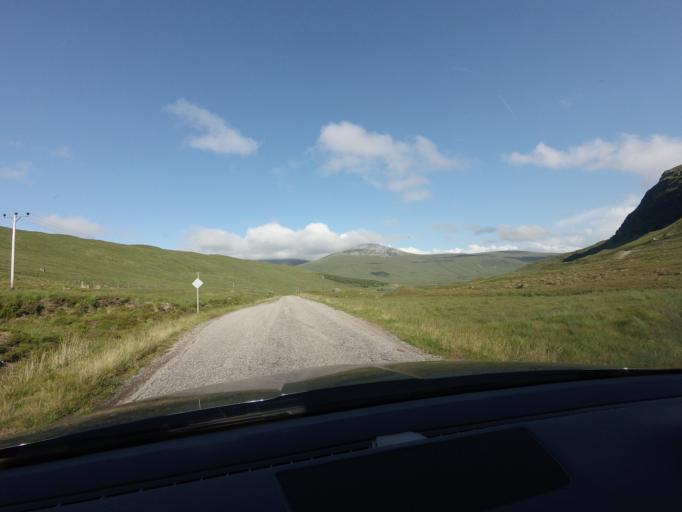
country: GB
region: Scotland
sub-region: Highland
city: Ullapool
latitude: 58.2573
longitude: -4.7868
